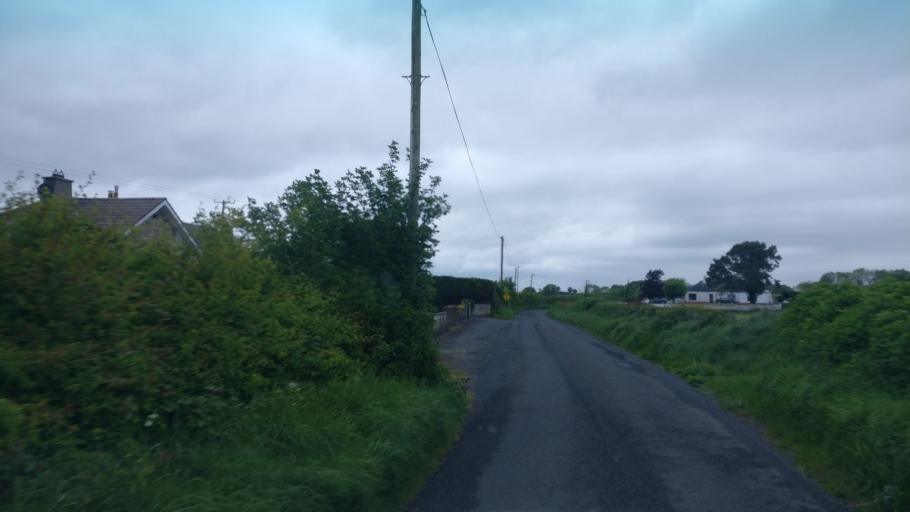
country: IE
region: Connaught
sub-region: County Galway
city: Portumna
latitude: 53.1161
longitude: -8.2887
